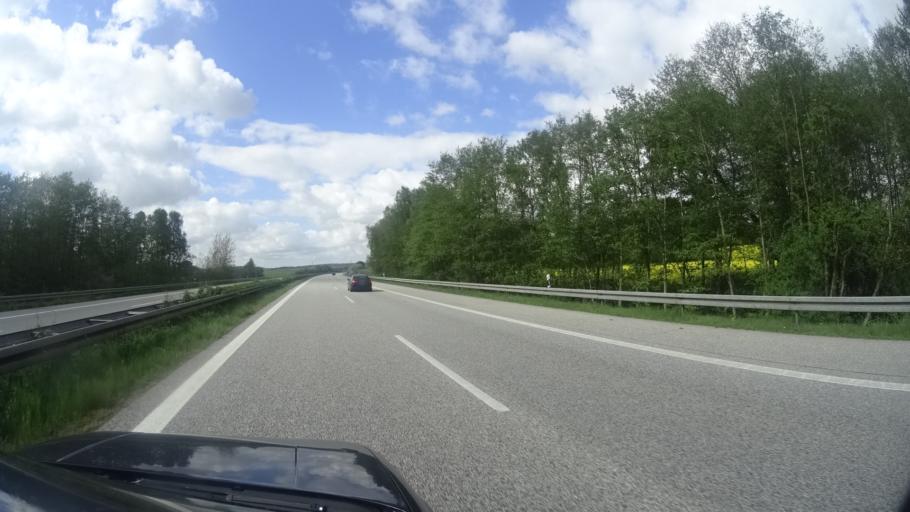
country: DE
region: Mecklenburg-Vorpommern
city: Muhl Rosin
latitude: 53.7976
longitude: 12.3005
